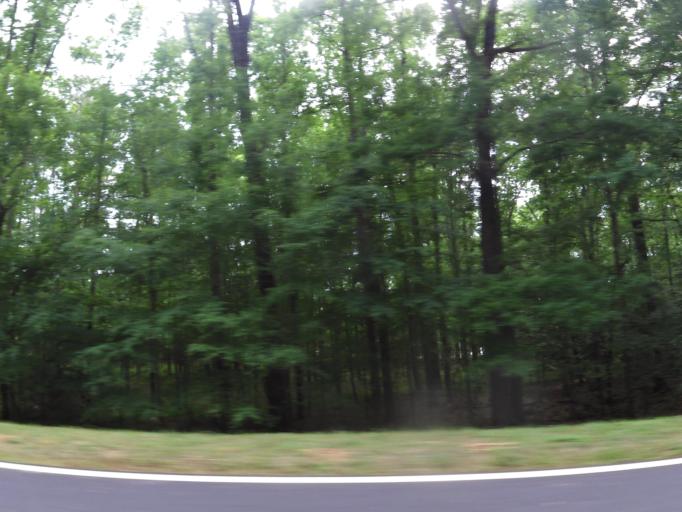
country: US
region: Georgia
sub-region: McDuffie County
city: Thomson
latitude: 33.5220
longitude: -82.4594
